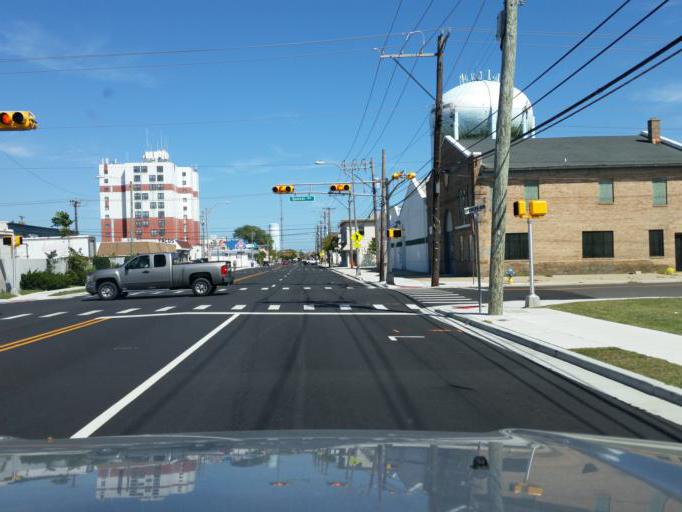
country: US
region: New Jersey
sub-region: Cape May County
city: Wildwood
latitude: 38.9882
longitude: -74.8189
